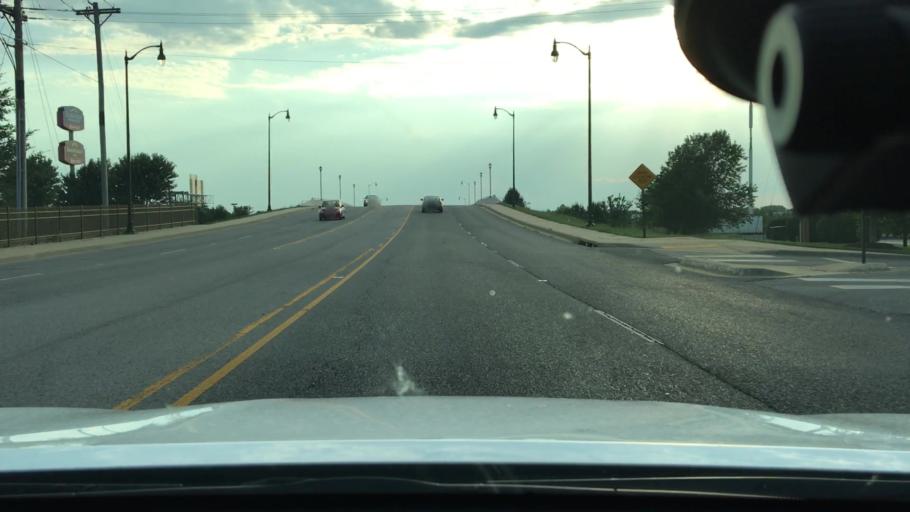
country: US
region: Arkansas
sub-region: Benton County
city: Bentonville
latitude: 36.3423
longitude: -94.1798
